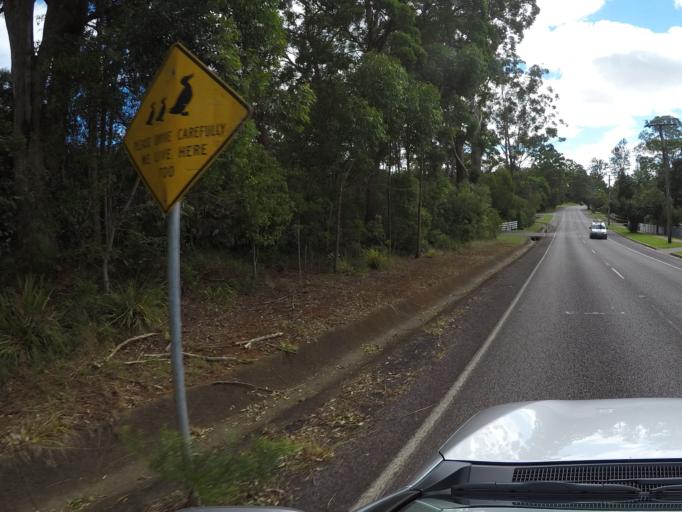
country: AU
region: Queensland
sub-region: Sunshine Coast
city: Nambour
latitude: -26.6292
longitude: 152.8598
